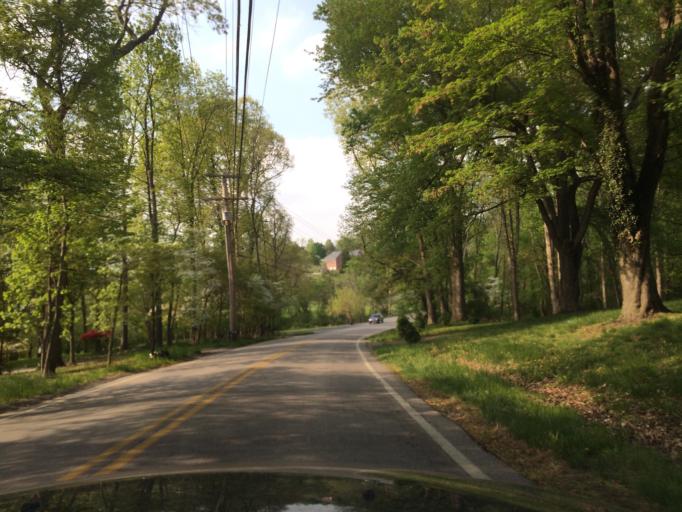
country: US
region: Maryland
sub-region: Howard County
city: Highland
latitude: 39.2037
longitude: -76.9819
